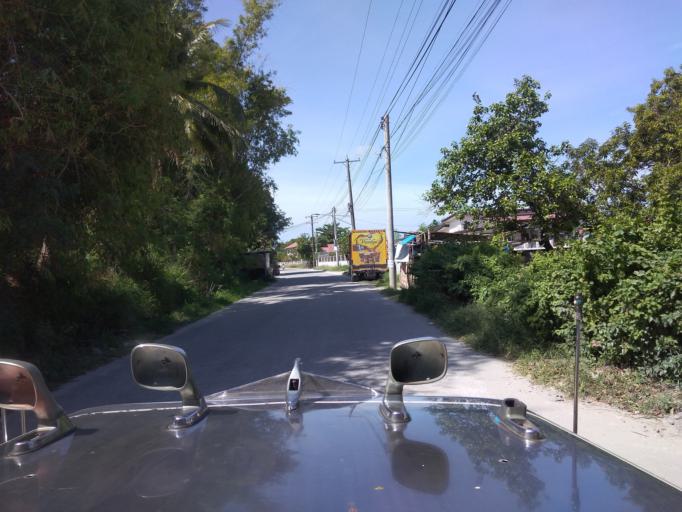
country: PH
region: Central Luzon
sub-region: Province of Pampanga
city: Bacolor
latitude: 15.0174
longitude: 120.6593
